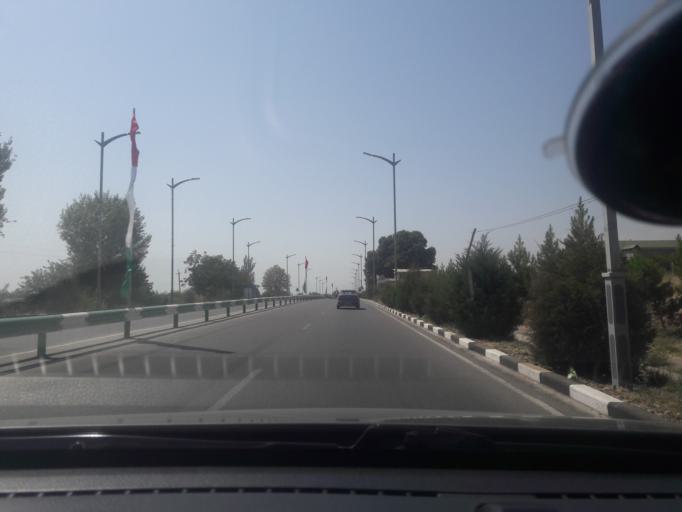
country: TJ
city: Shahrinav
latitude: 38.5612
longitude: 68.4399
